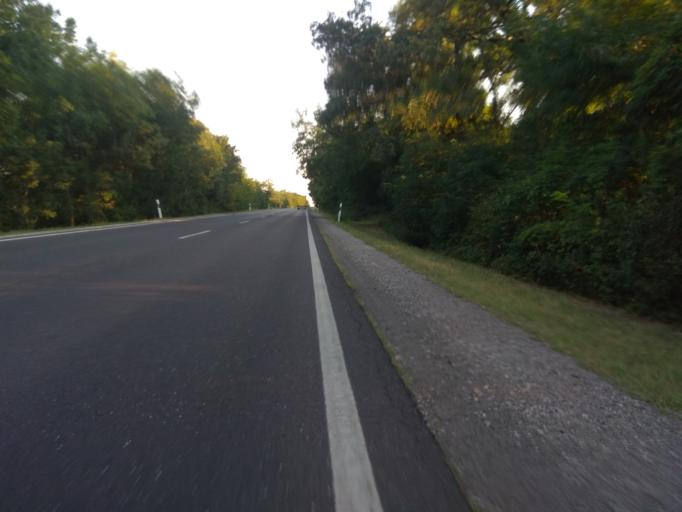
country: HU
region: Borsod-Abauj-Zemplen
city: Nyekladhaza
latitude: 47.9569
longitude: 20.8344
